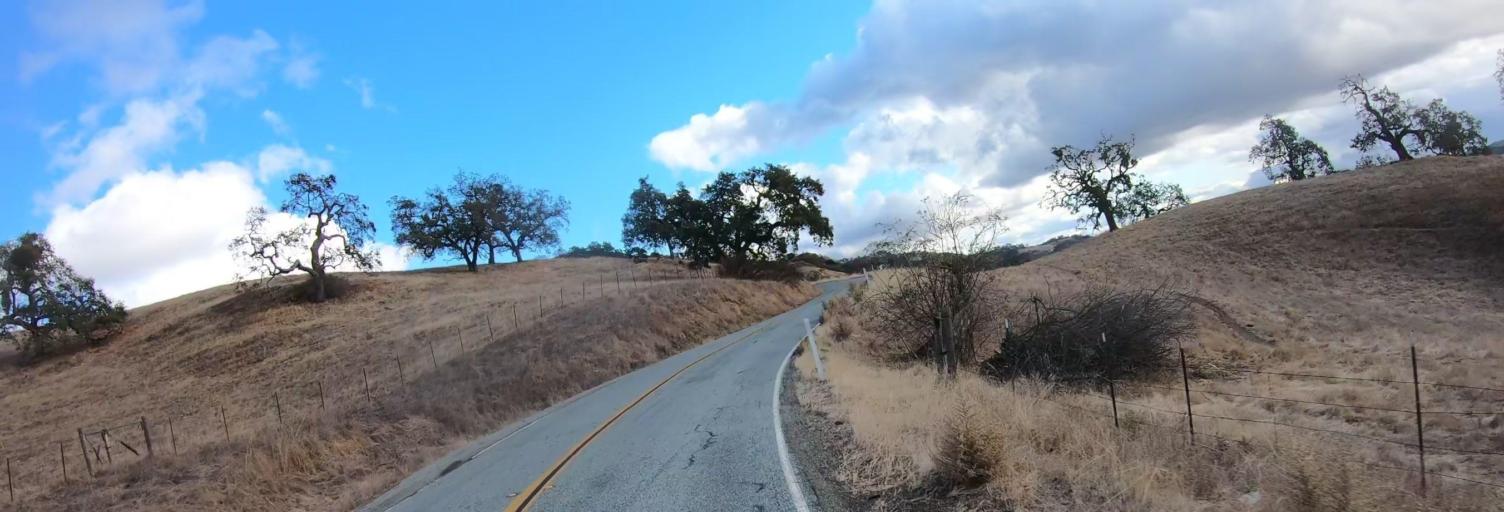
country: US
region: California
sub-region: Santa Clara County
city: East Foothills
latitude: 37.3351
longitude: -121.7027
